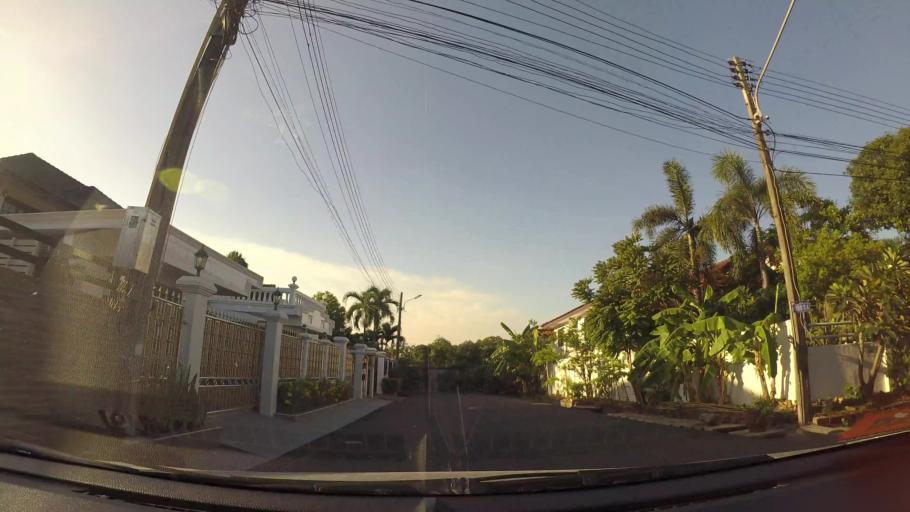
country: TH
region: Chon Buri
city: Si Racha
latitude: 13.1403
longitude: 100.9338
